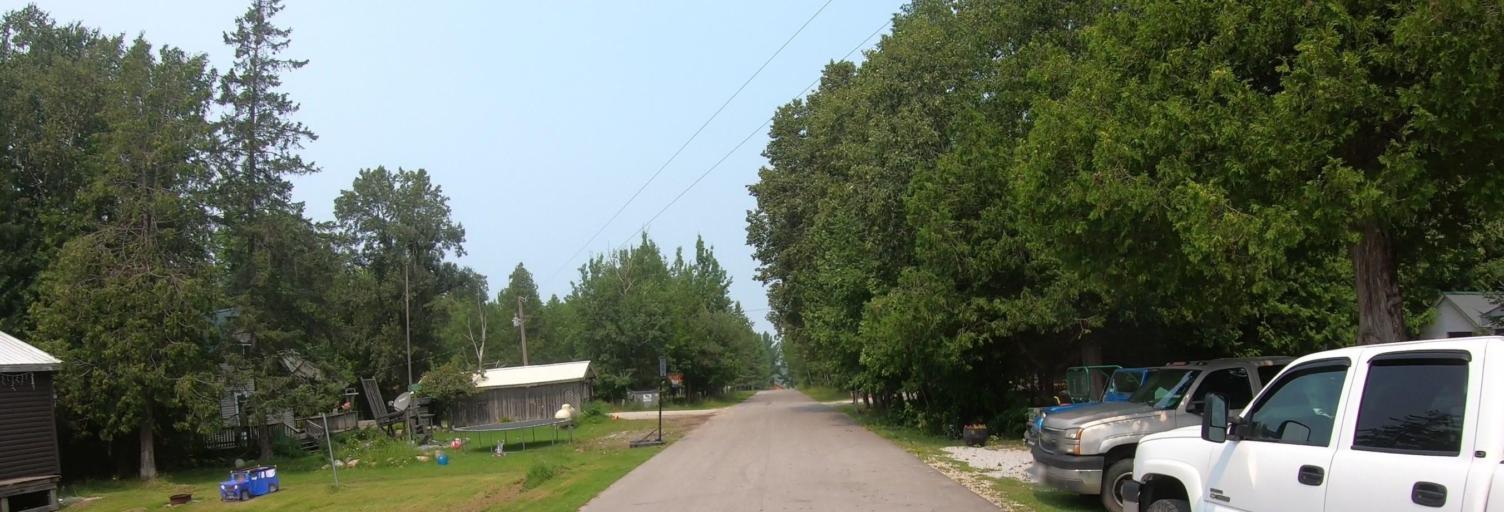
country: CA
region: Ontario
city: Thessalon
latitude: 46.0315
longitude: -83.6771
